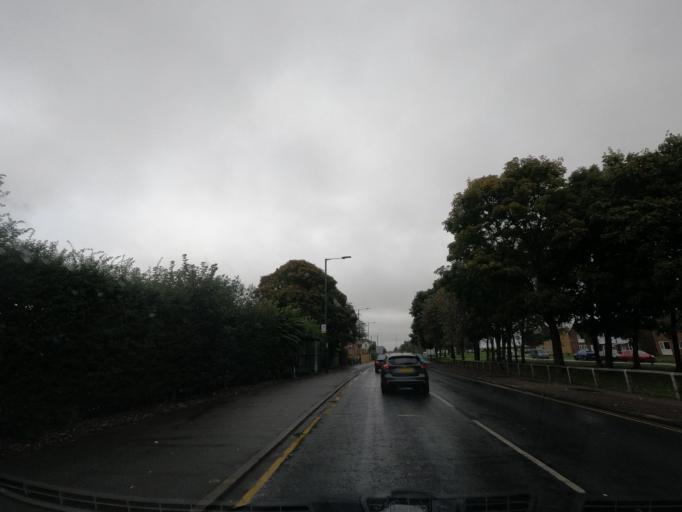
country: GB
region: England
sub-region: Middlesbrough
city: Nunthorpe
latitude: 54.5484
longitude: -1.1791
